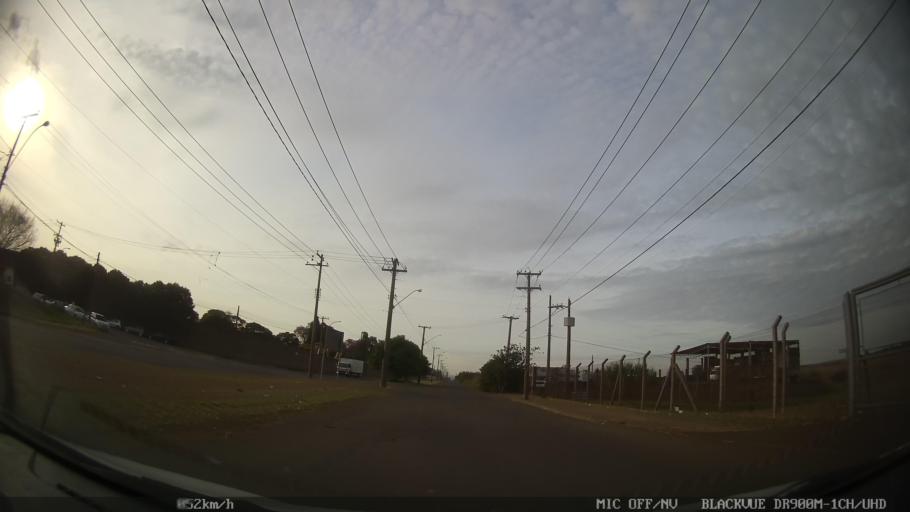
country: BR
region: Sao Paulo
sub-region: Piracicaba
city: Piracicaba
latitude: -22.7312
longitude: -47.5874
